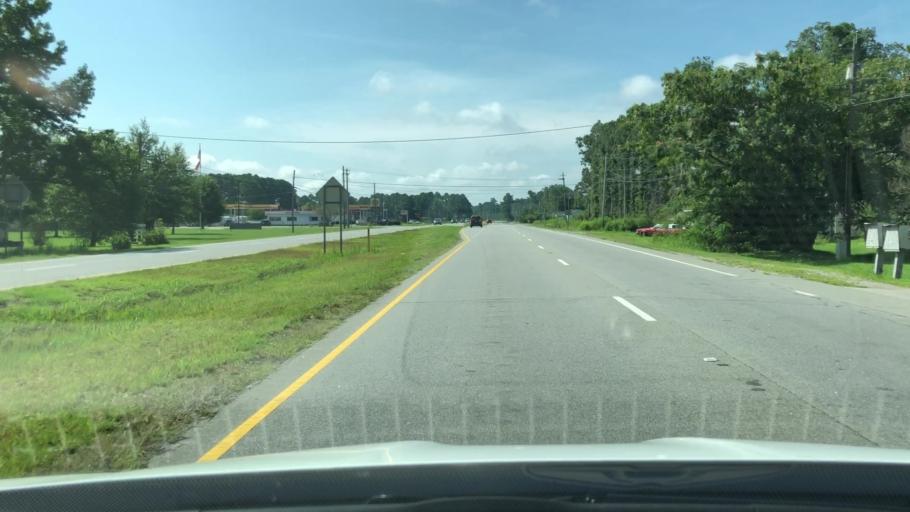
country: US
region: North Carolina
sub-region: Bertie County
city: Windsor
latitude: 35.9820
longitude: -76.9571
